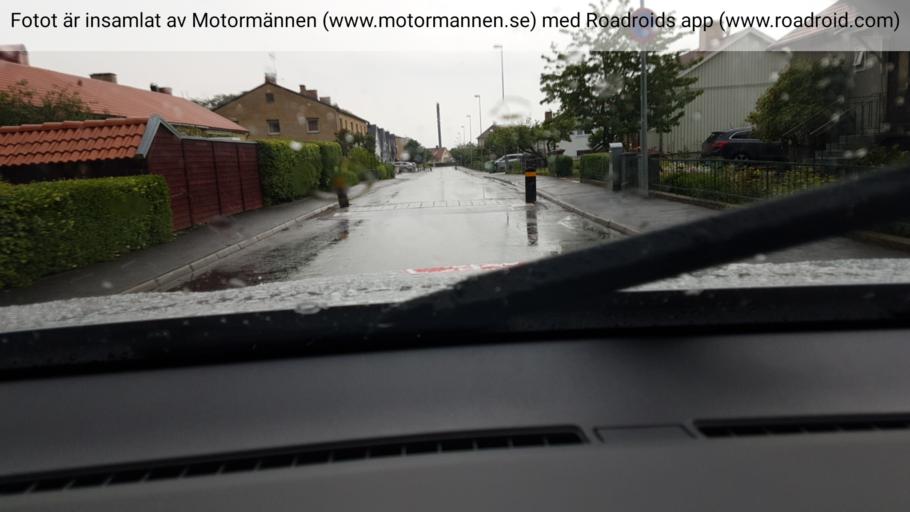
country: SE
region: Vaestra Goetaland
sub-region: Skovde Kommun
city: Skoevde
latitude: 58.4013
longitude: 13.8558
